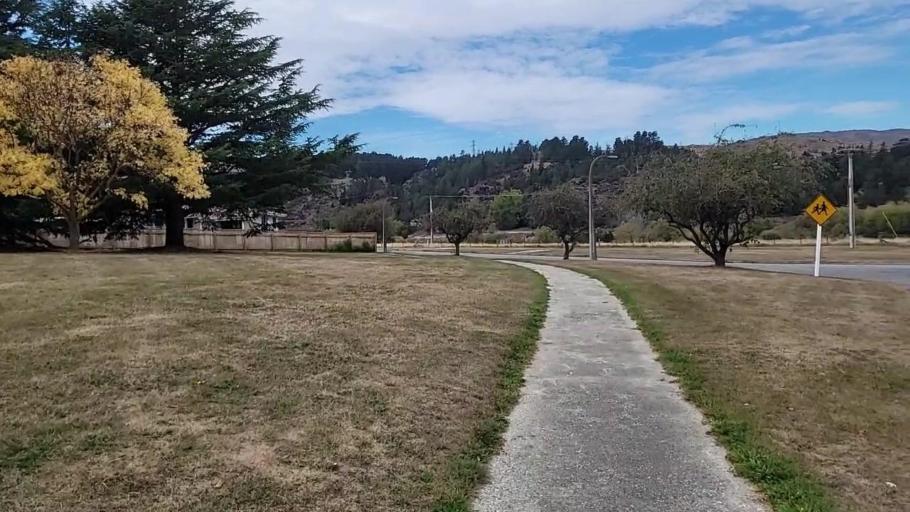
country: NZ
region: Otago
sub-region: Queenstown-Lakes District
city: Kingston
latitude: -45.4805
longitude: 169.3136
